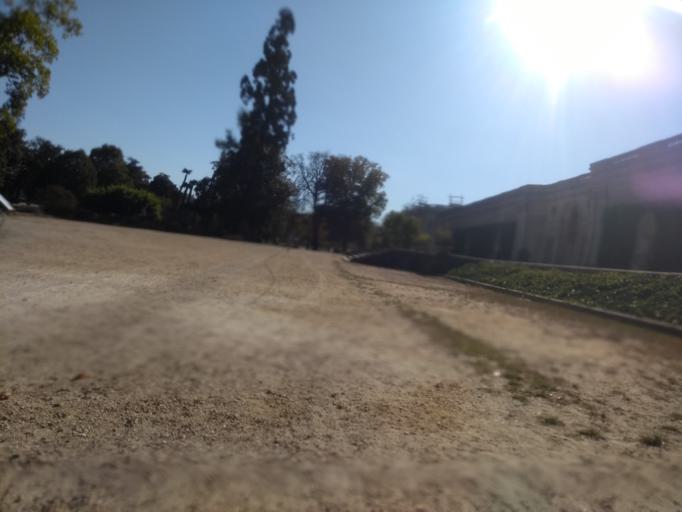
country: FR
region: Aquitaine
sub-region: Departement de la Gironde
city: Bordeaux
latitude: 44.8495
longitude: -0.5789
